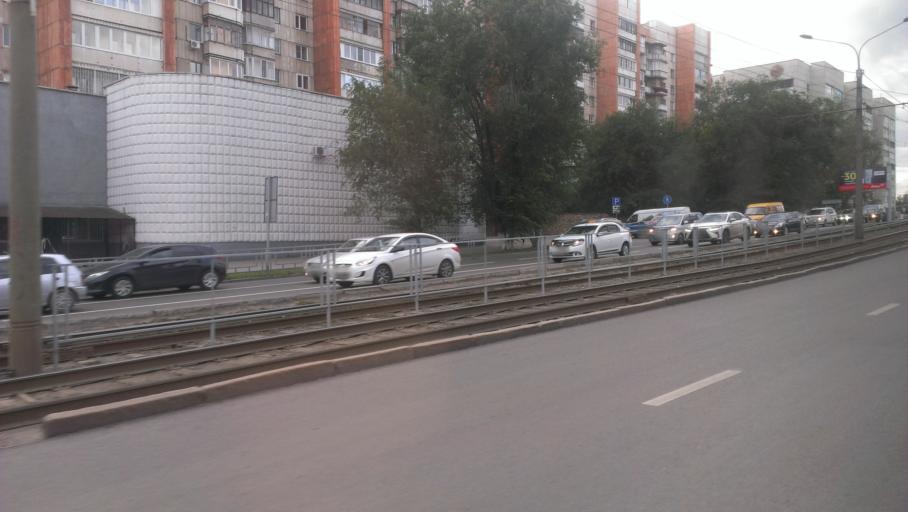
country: RU
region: Altai Krai
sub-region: Gorod Barnaulskiy
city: Barnaul
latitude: 53.3430
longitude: 83.7686
